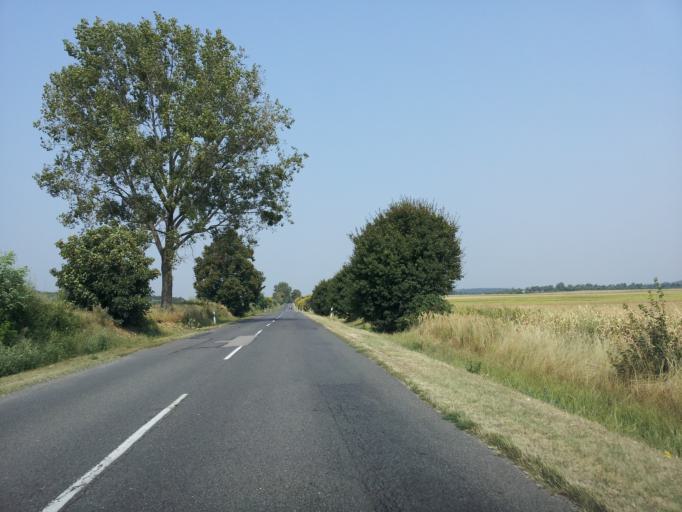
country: HU
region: Gyor-Moson-Sopron
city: Pannonhalma
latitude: 47.4779
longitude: 17.7901
